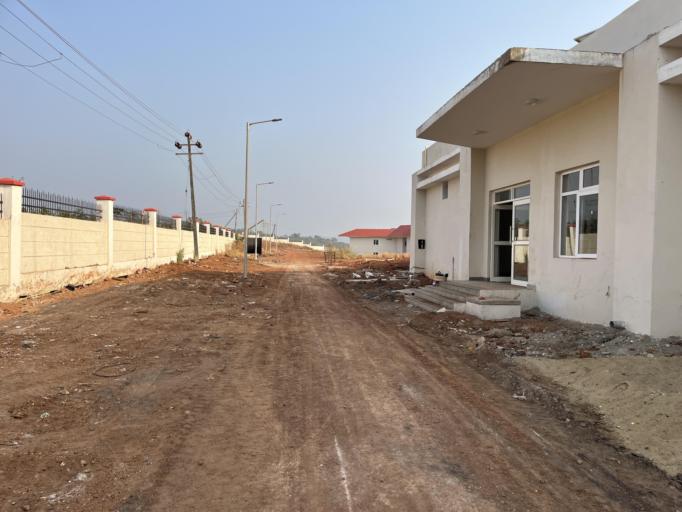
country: IN
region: Goa
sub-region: North Goa
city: Pernem
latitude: 15.6889
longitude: 73.8356
